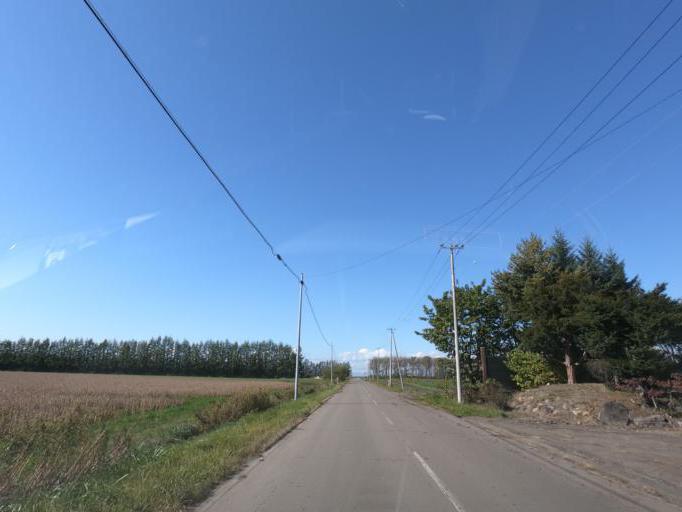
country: JP
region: Hokkaido
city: Otofuke
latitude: 43.0606
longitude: 143.2663
